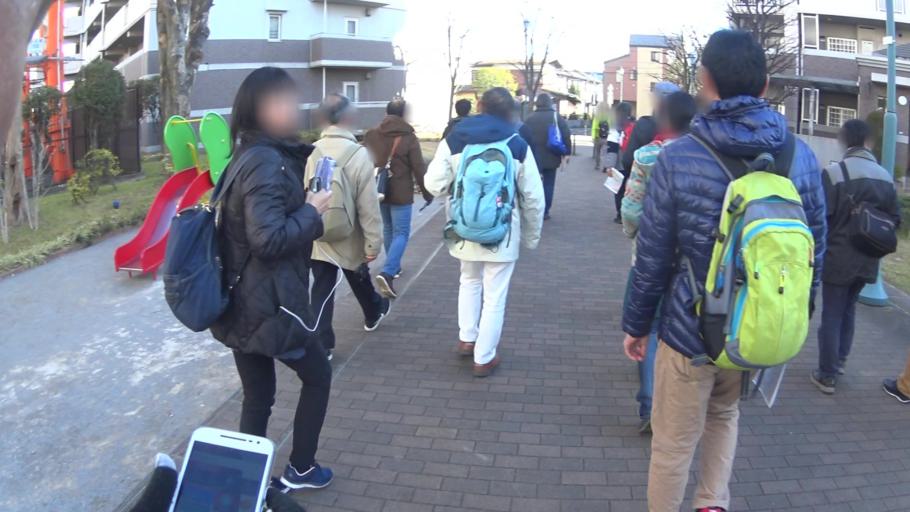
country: JP
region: Saitama
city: Shimotoda
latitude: 35.8439
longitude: 139.6766
